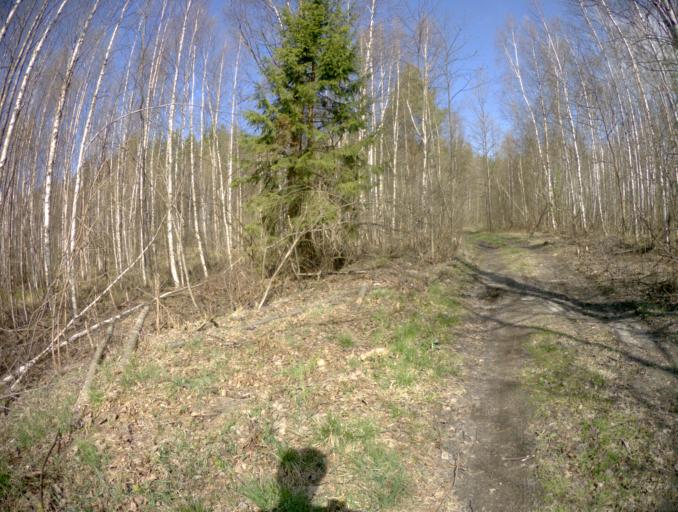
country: RU
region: Vladimir
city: Mezinovskiy
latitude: 55.5315
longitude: 40.2623
